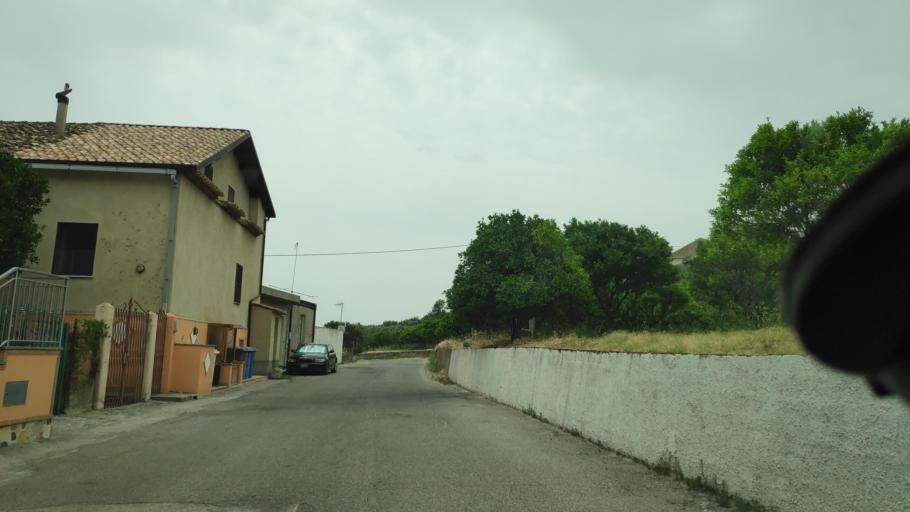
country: IT
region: Calabria
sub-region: Provincia di Catanzaro
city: Martelli-Laganosa
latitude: 38.6664
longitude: 16.5252
